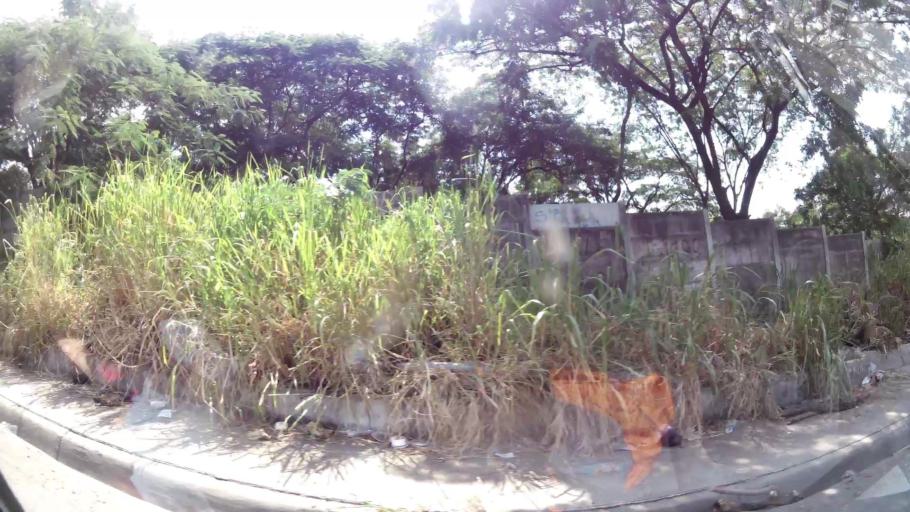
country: EC
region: Guayas
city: Guayaquil
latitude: -2.1172
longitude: -79.9245
